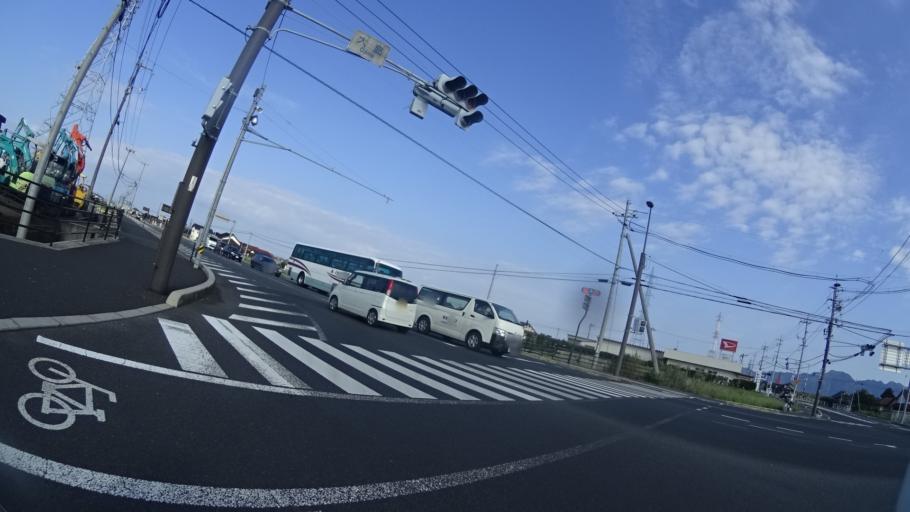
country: JP
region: Shimane
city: Izumo
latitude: 35.3376
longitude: 132.7020
